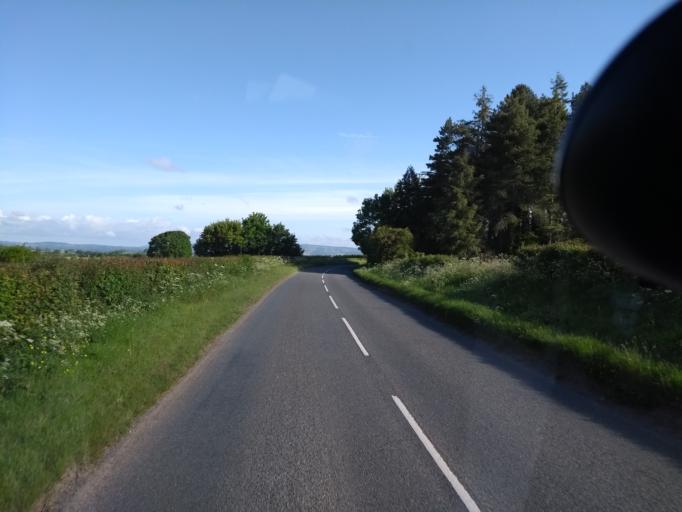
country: GB
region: England
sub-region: Somerset
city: Taunton
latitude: 50.9705
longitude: -3.1259
